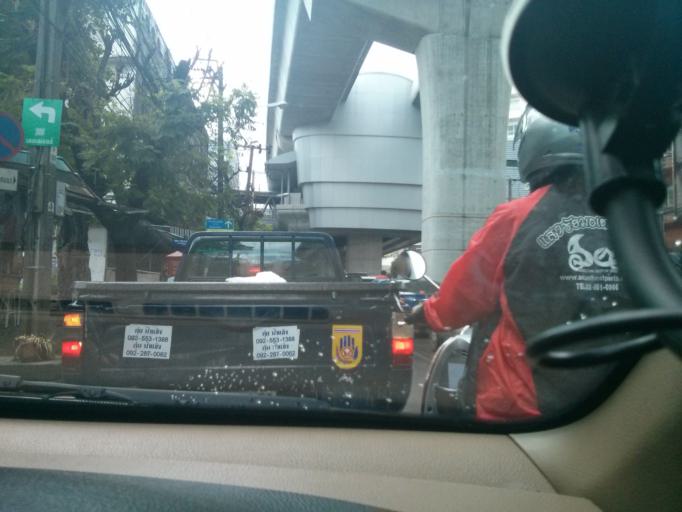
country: TH
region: Nonthaburi
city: Mueang Nonthaburi
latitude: 13.8408
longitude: 100.5136
